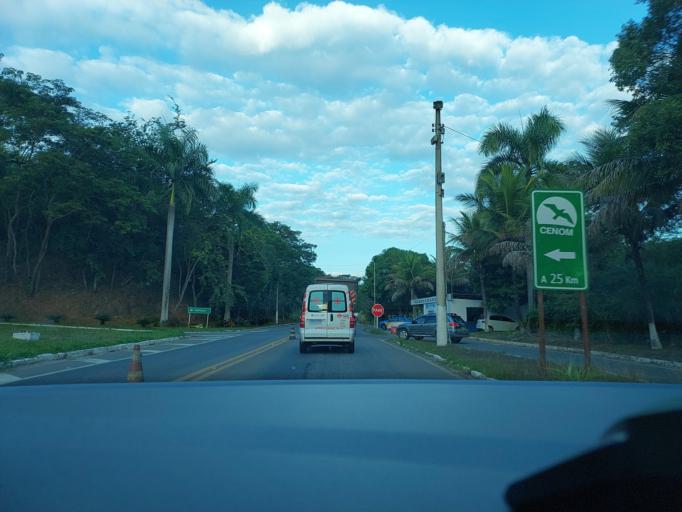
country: BR
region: Minas Gerais
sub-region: Muriae
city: Muriae
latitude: -21.1460
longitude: -42.1682
